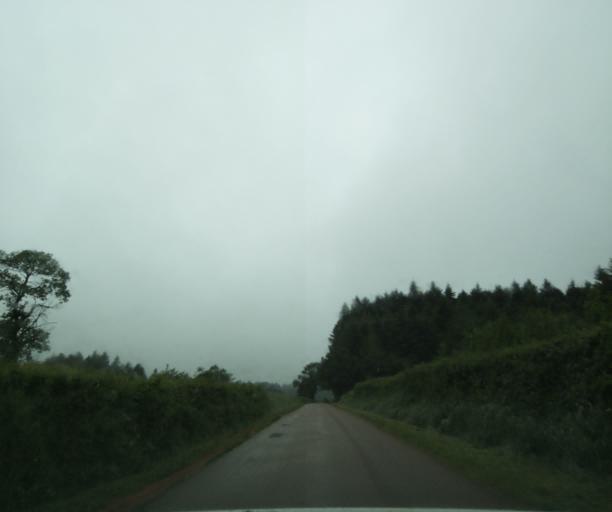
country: FR
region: Bourgogne
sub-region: Departement de Saone-et-Loire
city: Matour
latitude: 46.4033
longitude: 4.4152
